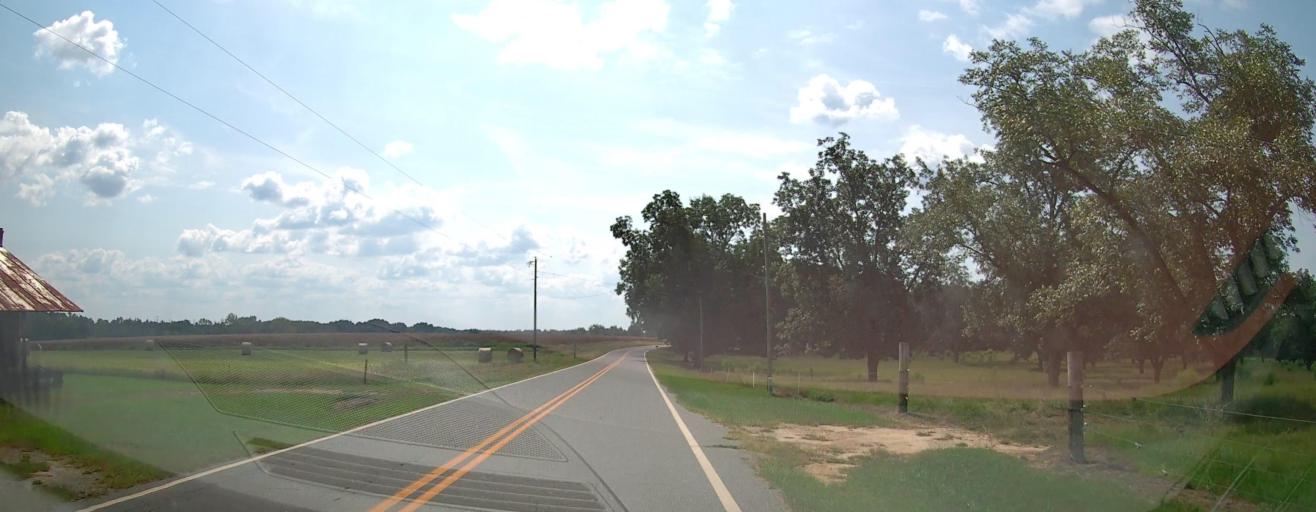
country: US
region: Georgia
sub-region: Bleckley County
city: Cochran
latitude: 32.5261
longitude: -83.3078
